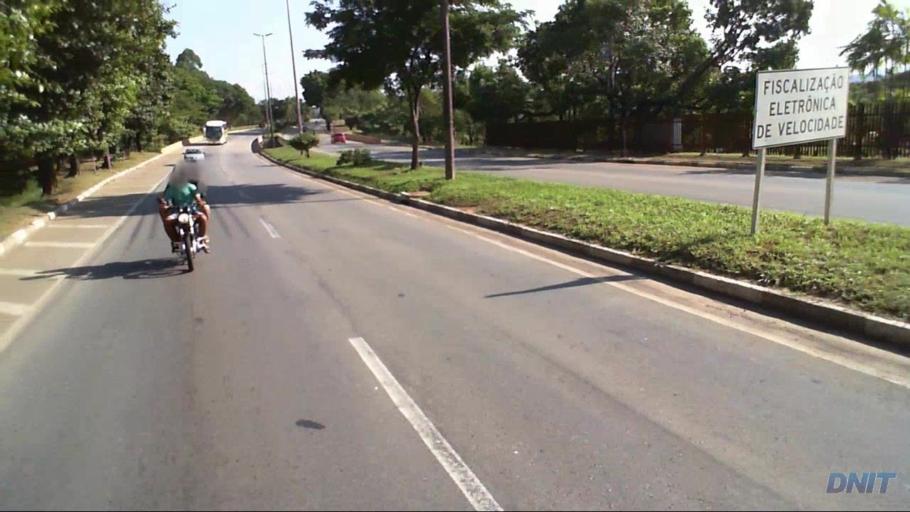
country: BR
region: Minas Gerais
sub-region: Ipatinga
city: Ipatinga
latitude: -19.4688
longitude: -42.5375
